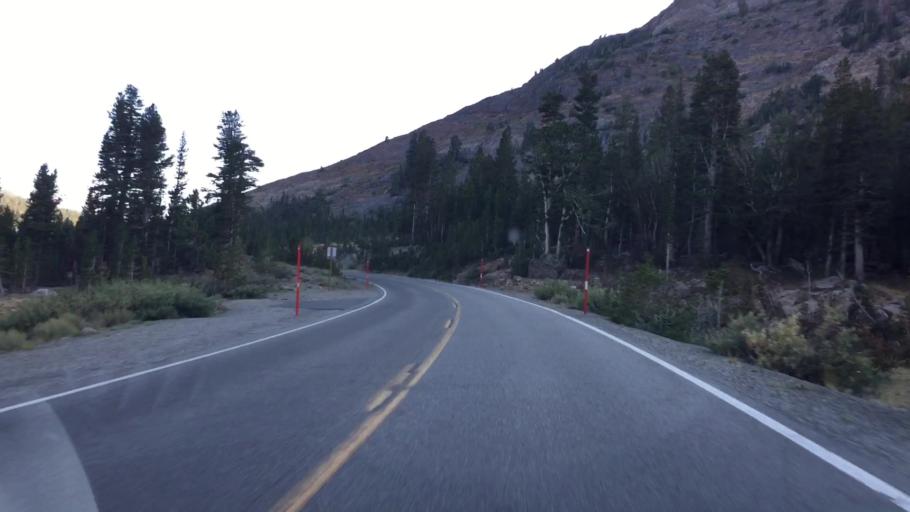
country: US
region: California
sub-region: Mono County
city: Bridgeport
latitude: 37.9260
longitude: -119.2563
